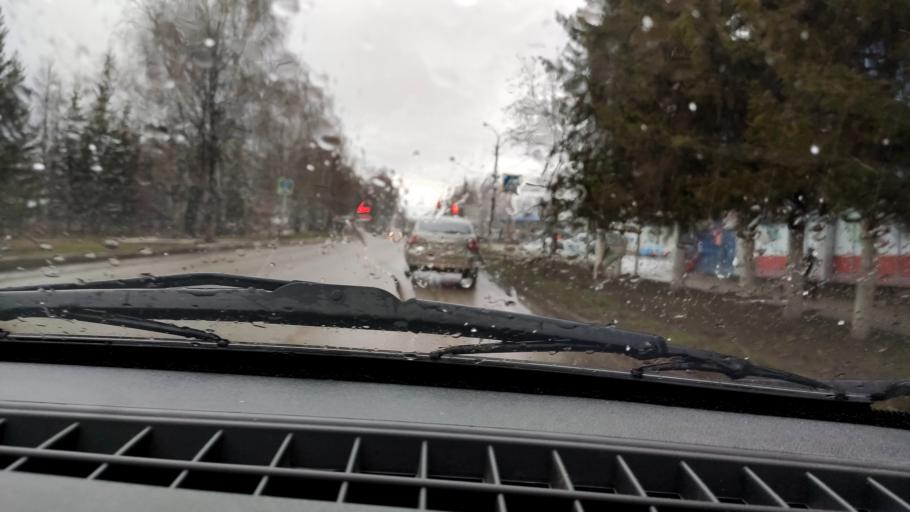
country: RU
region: Bashkortostan
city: Chekmagush
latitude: 55.1388
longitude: 54.6528
